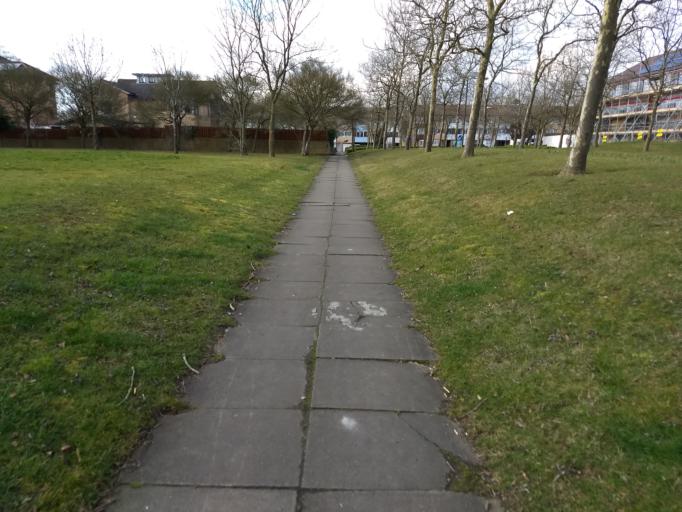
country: GB
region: England
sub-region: Milton Keynes
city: Milton Keynes
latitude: 52.0363
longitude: -0.7436
